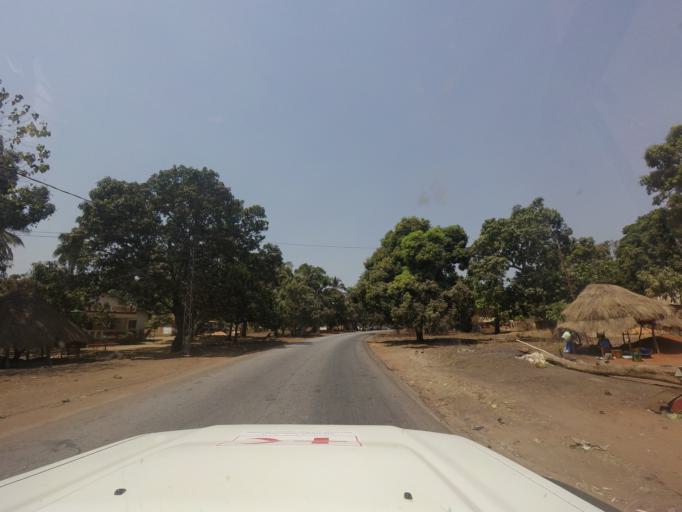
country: GN
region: Kindia
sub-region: Kindia
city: Kindia
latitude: 9.9505
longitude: -12.9492
